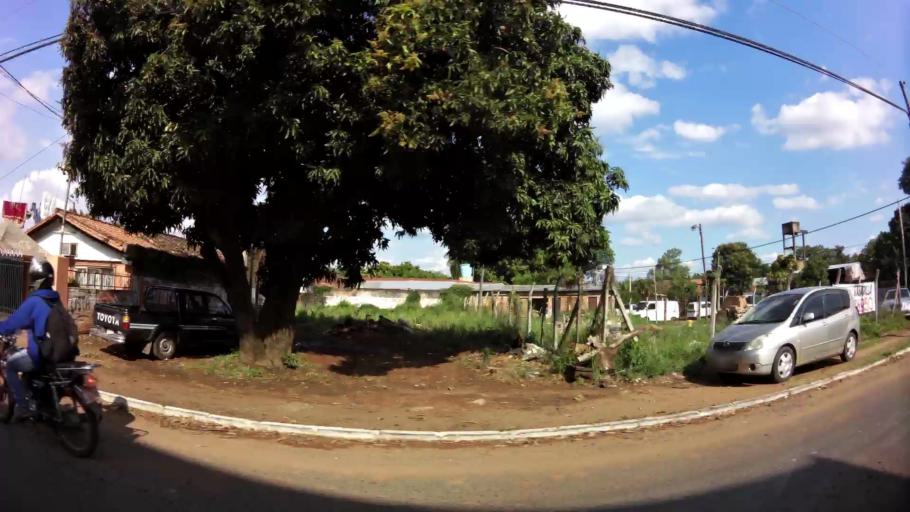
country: PY
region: Central
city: Fernando de la Mora
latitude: -25.3325
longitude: -57.5312
